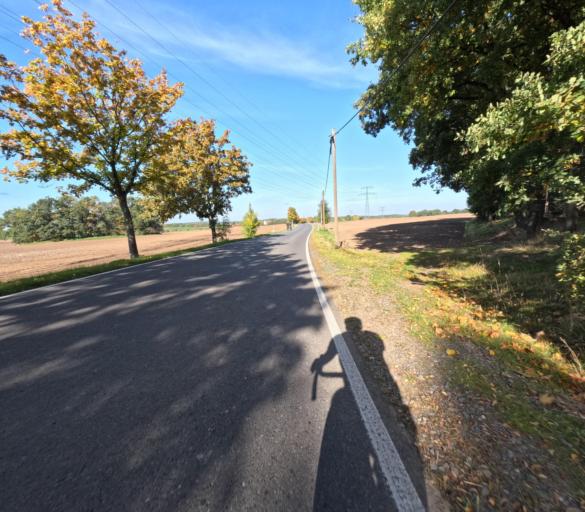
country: DE
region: Saxony
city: Ottendorf-Okrilla
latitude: 51.1578
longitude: 13.7779
